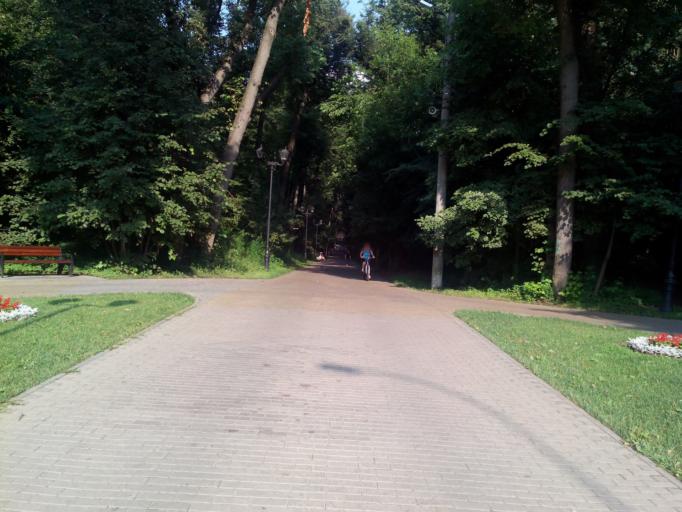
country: RU
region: Moskovskaya
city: Fili
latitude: 55.7505
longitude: 37.4797
